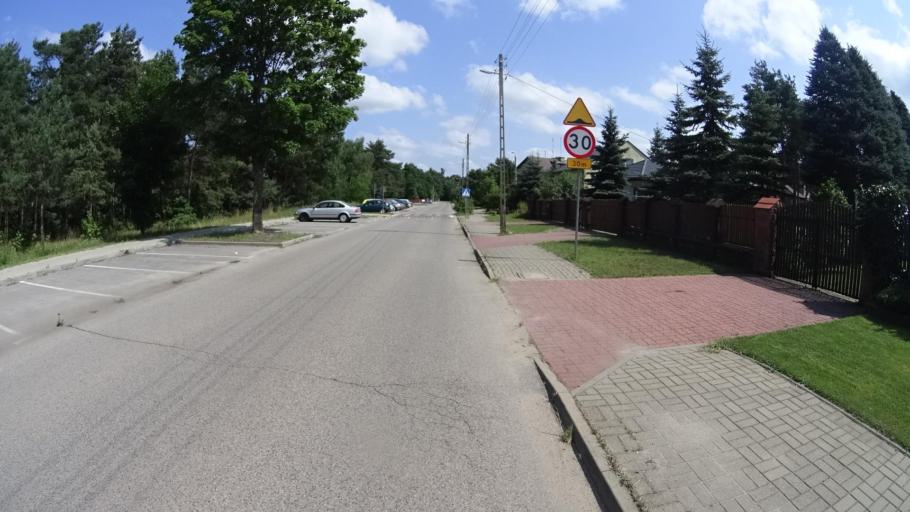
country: PL
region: Masovian Voivodeship
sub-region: Powiat bialobrzeski
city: Bialobrzegi
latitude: 51.6461
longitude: 20.9609
